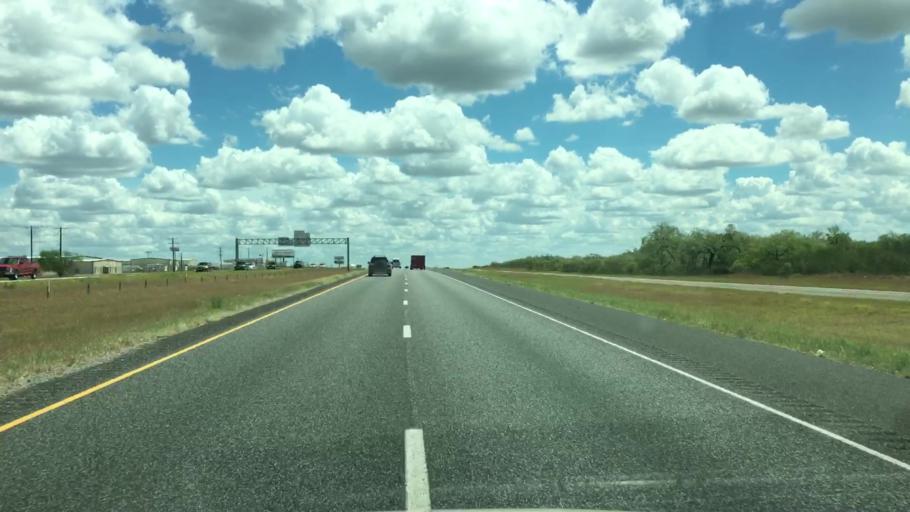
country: US
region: Texas
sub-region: Atascosa County
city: Pleasanton
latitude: 28.8935
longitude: -98.4129
